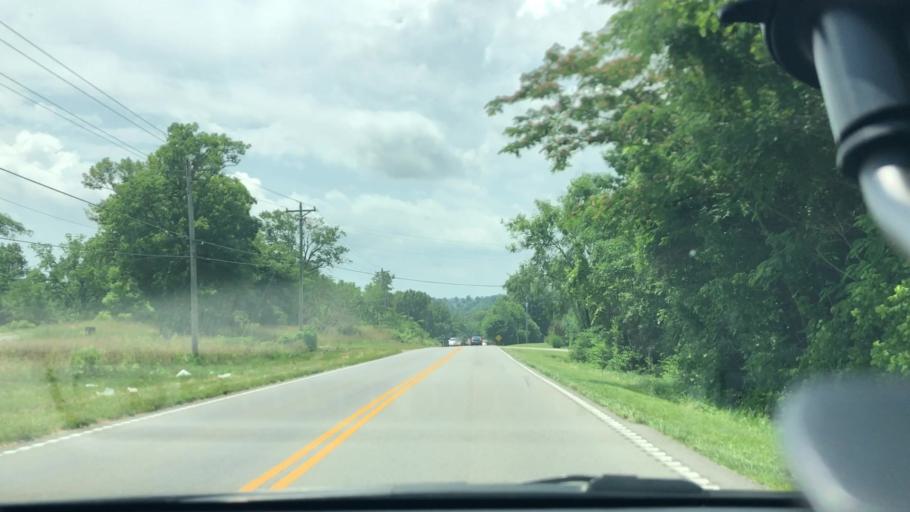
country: US
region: Kentucky
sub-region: Pulaski County
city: Somerset
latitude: 37.0582
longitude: -84.6759
